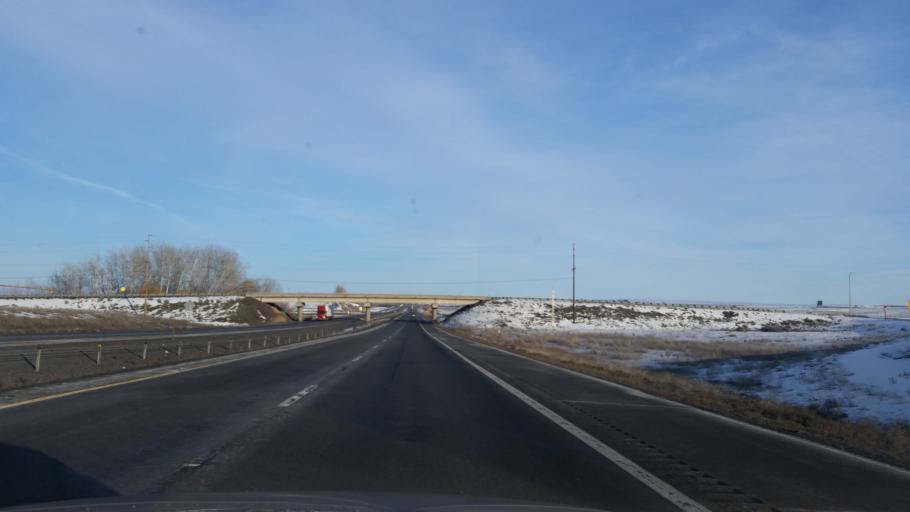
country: US
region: Washington
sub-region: Grant County
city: Warden
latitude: 47.0857
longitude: -119.0476
